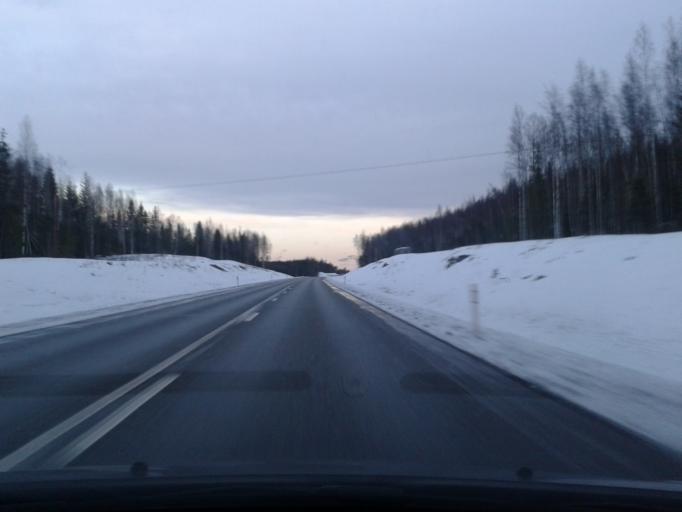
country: SE
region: Vaesternorrland
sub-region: Kramfors Kommun
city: Bollstabruk
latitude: 63.0591
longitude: 17.6051
